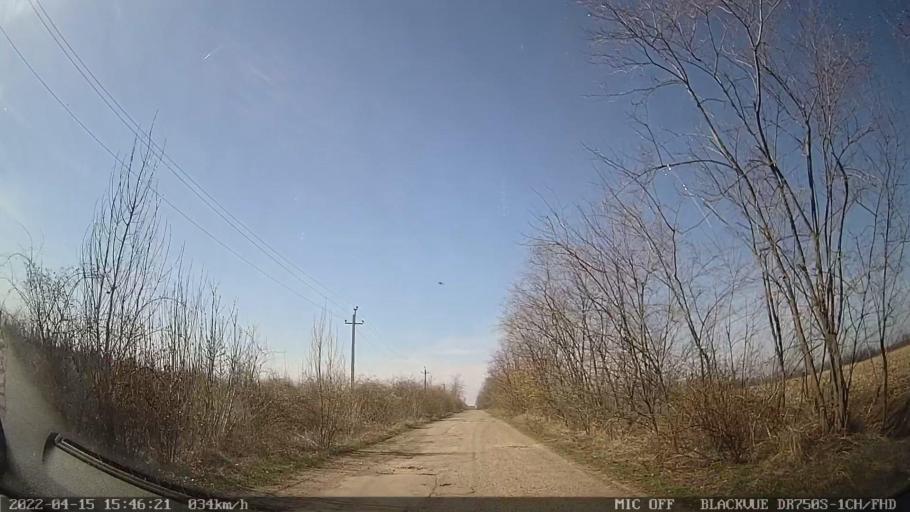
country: MD
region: Raionul Ocnita
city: Otaci
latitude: 48.3809
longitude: 27.9139
